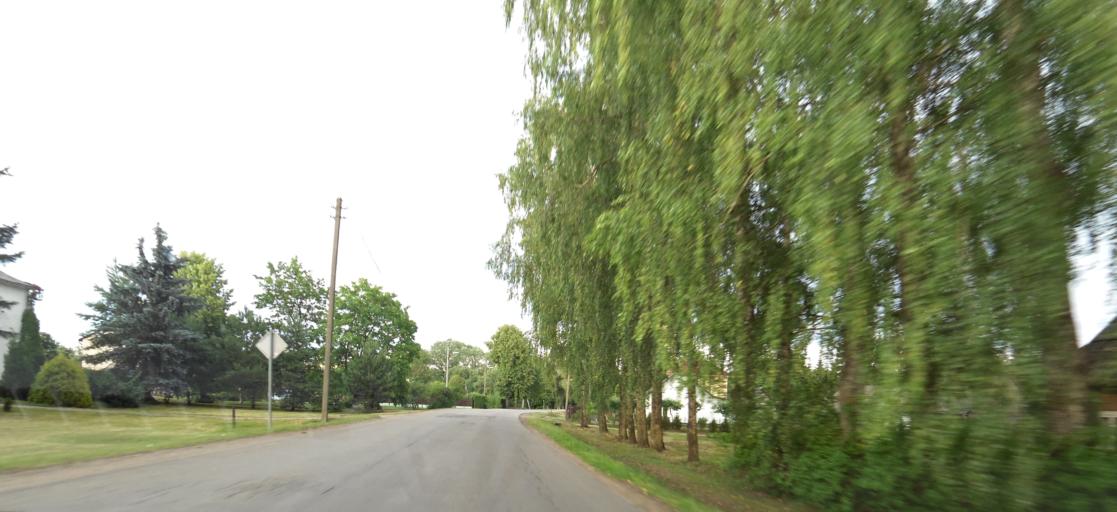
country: LT
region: Panevezys
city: Pasvalys
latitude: 56.0694
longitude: 24.4458
